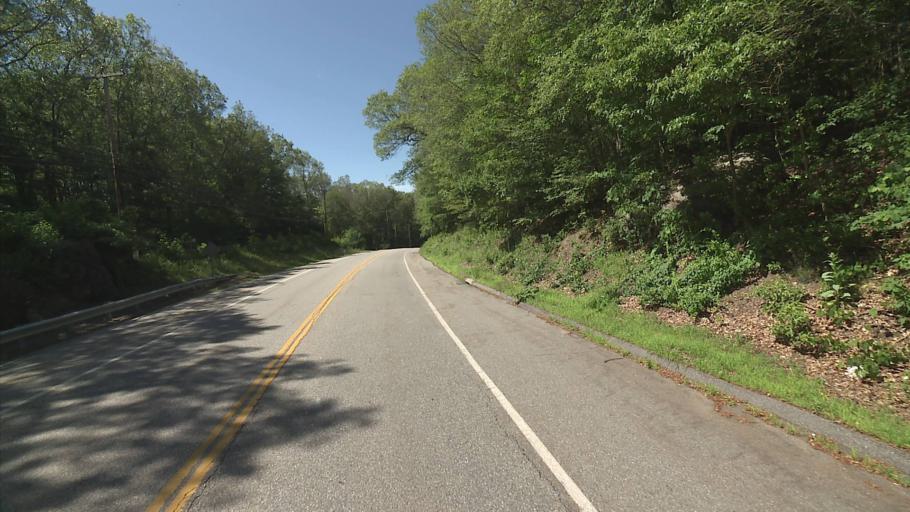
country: US
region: Connecticut
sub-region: Windham County
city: Willimantic
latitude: 41.6997
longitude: -72.2180
